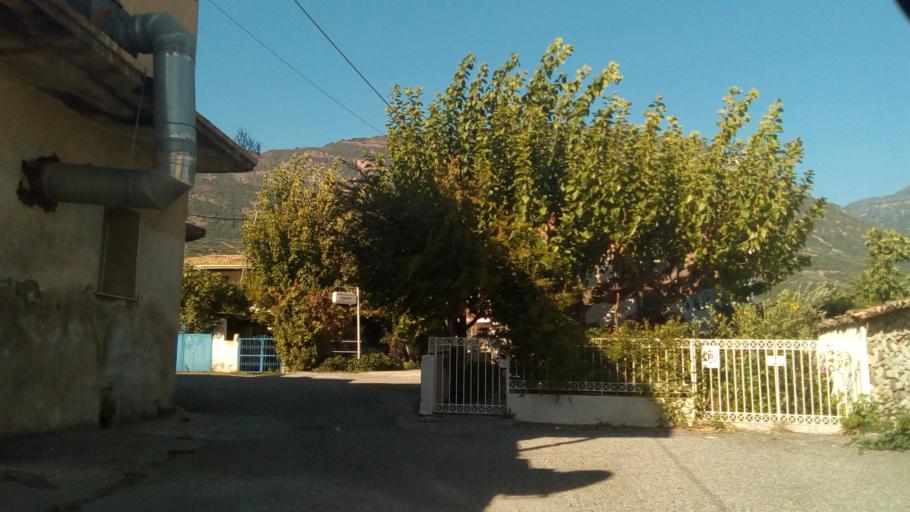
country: GR
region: West Greece
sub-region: Nomos Achaias
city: Selianitika
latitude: 38.3807
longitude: 22.0759
